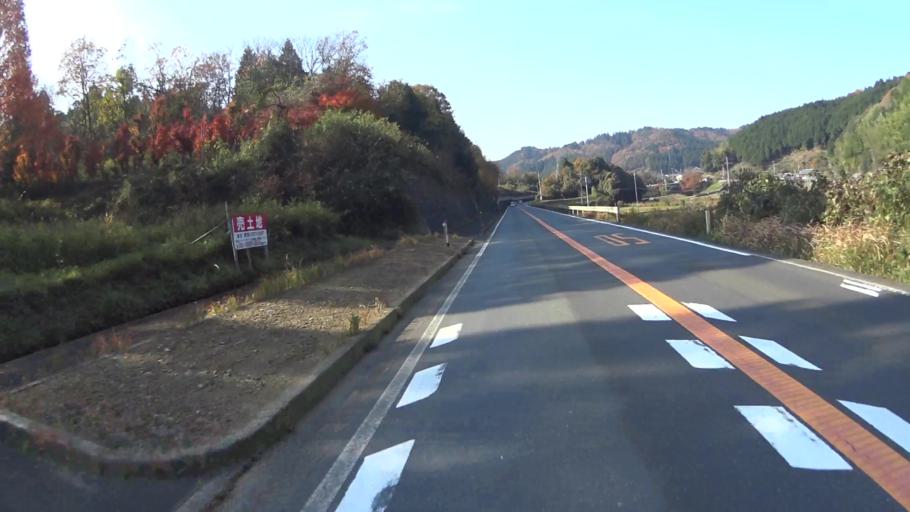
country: JP
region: Kyoto
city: Ayabe
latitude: 35.1902
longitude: 135.3014
